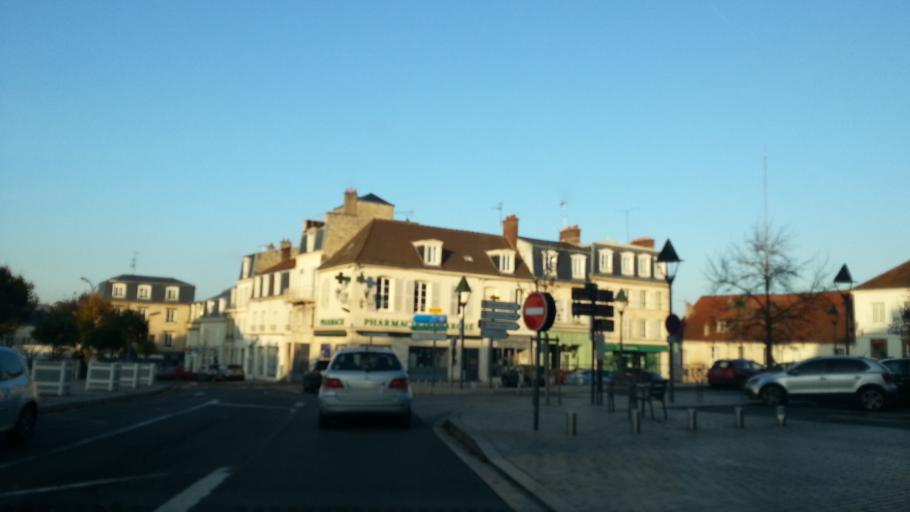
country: FR
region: Picardie
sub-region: Departement de l'Oise
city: Chantilly
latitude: 49.1940
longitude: 2.4657
